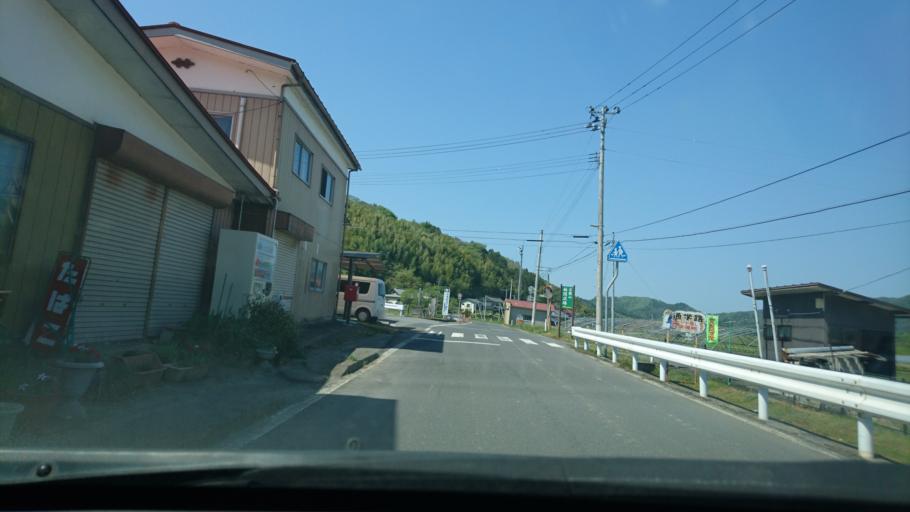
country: JP
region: Iwate
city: Ichinoseki
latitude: 38.9361
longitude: 141.2451
